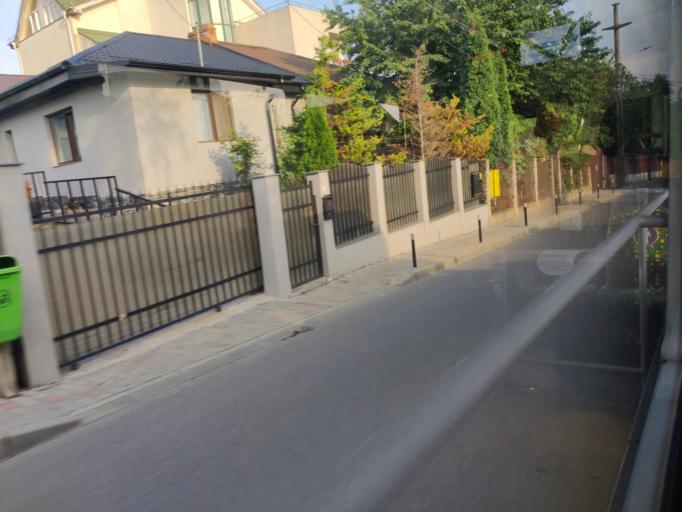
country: RO
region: Iasi
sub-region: Municipiul Iasi
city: Iasi
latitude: 47.1712
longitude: 27.5996
